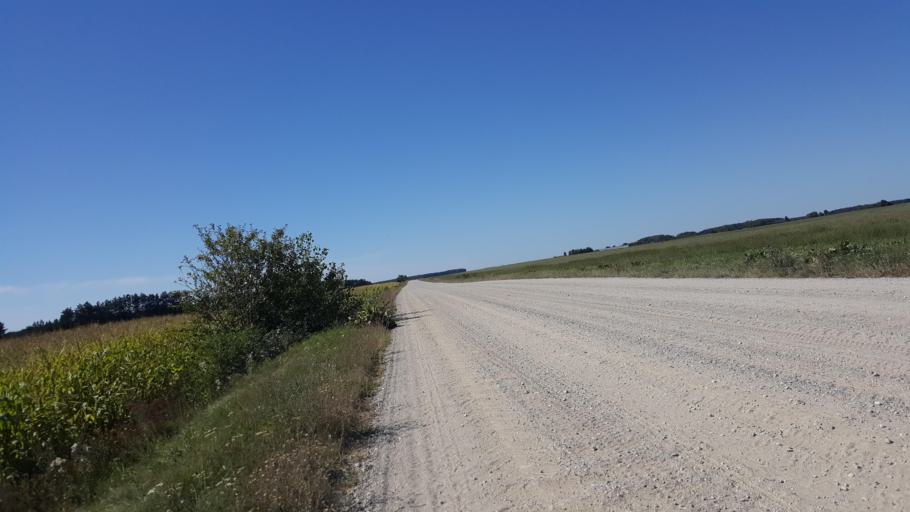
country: PL
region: Lublin Voivodeship
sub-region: Powiat bialski
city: Rokitno
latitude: 52.2276
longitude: 23.3264
